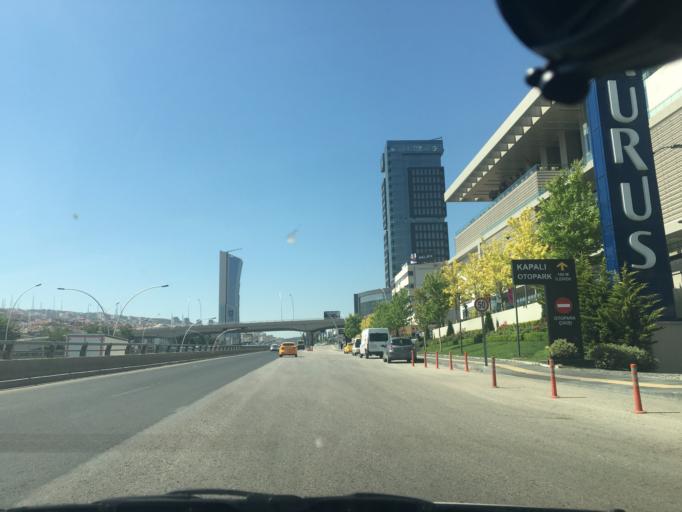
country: TR
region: Ankara
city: Ankara
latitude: 39.8890
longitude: 32.8124
